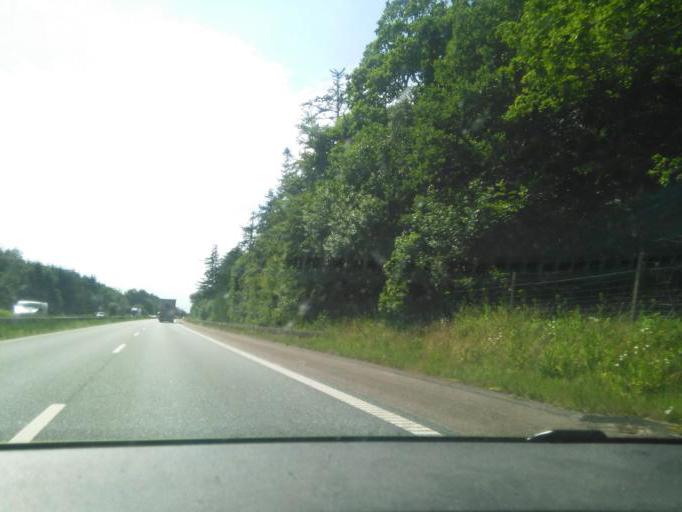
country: DK
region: Zealand
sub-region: Soro Kommune
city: Soro
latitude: 55.4374
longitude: 11.4989
